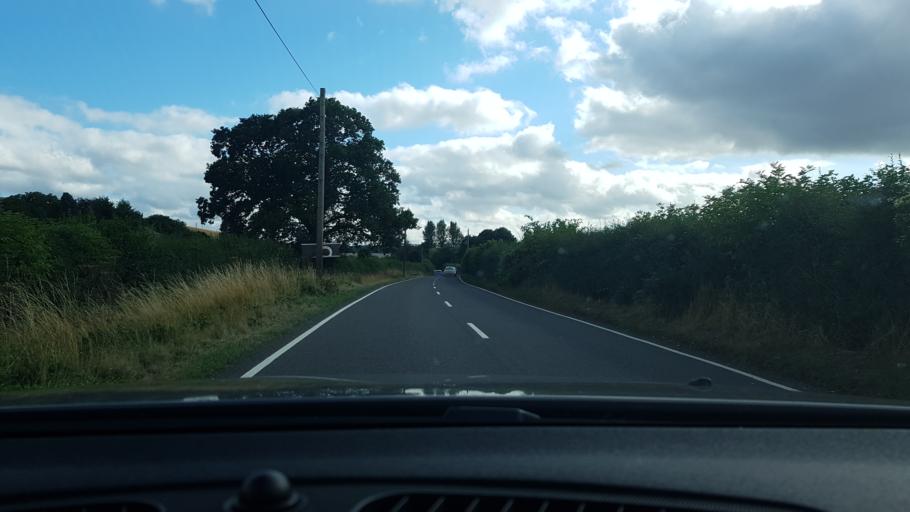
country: GB
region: England
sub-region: West Berkshire
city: Welford
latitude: 51.4846
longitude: -1.4380
